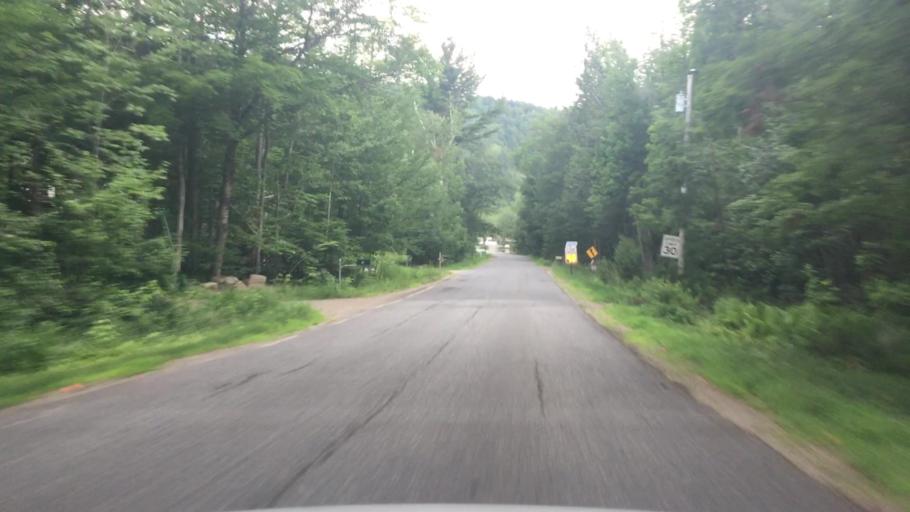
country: US
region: Maine
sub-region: Knox County
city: Washington
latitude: 44.3728
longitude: -69.3489
